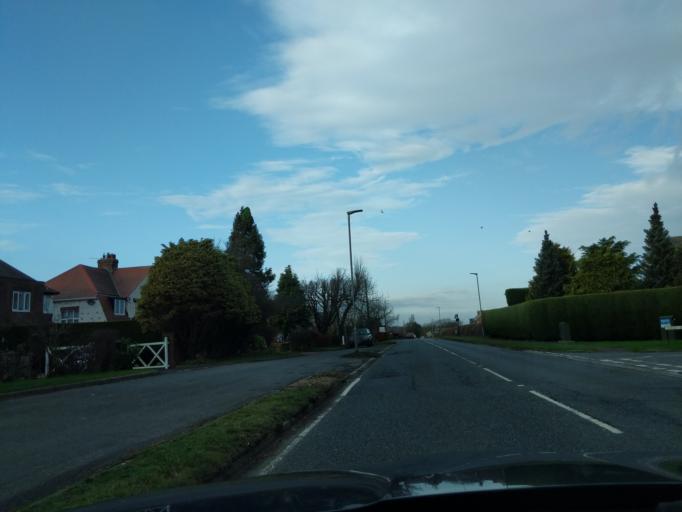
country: GB
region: England
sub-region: Northumberland
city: Ponteland
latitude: 55.0468
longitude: -1.7315
